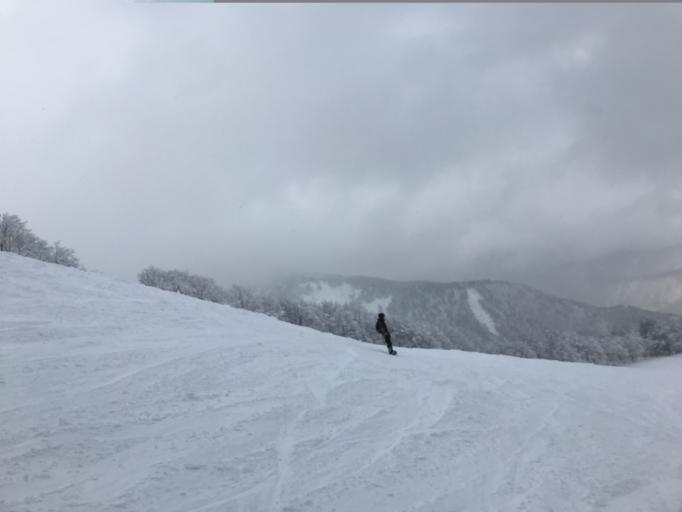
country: JP
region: Nagano
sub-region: Kitaazumi Gun
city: Hakuba
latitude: 36.7071
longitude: 137.8125
